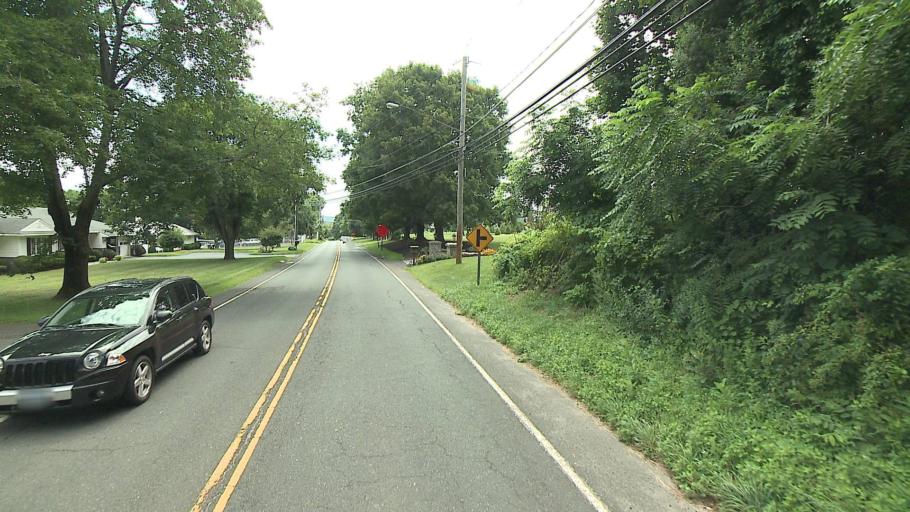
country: US
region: Connecticut
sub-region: Fairfield County
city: Danbury
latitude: 41.4125
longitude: -73.4703
